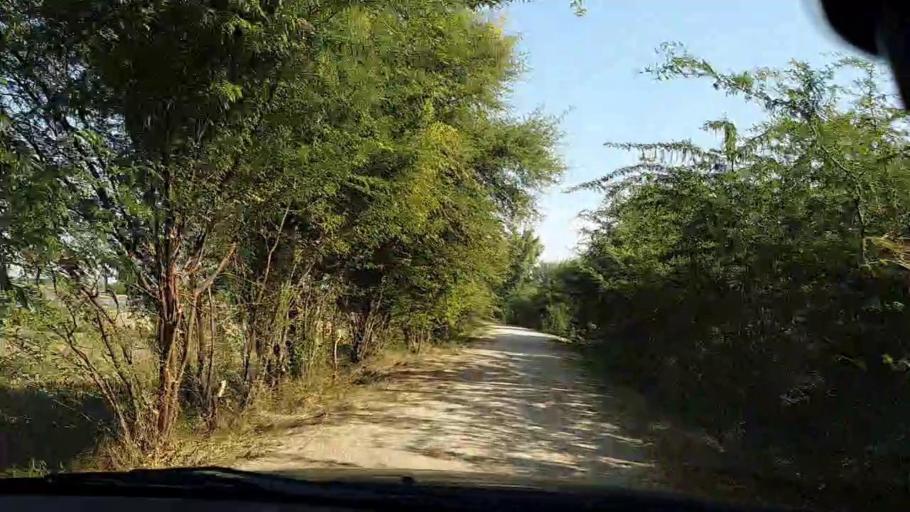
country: PK
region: Sindh
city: Mirpur Batoro
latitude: 24.6293
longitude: 68.2667
